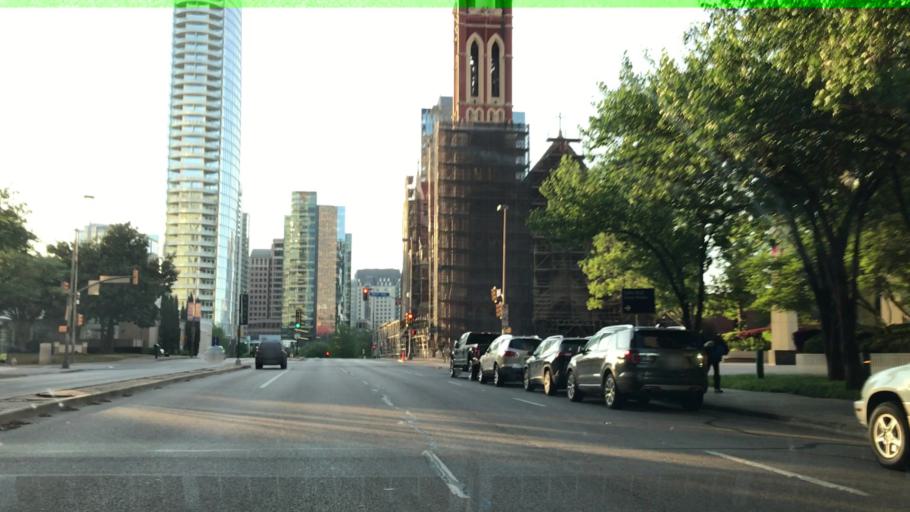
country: US
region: Texas
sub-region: Dallas County
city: Dallas
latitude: 32.7877
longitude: -96.7971
